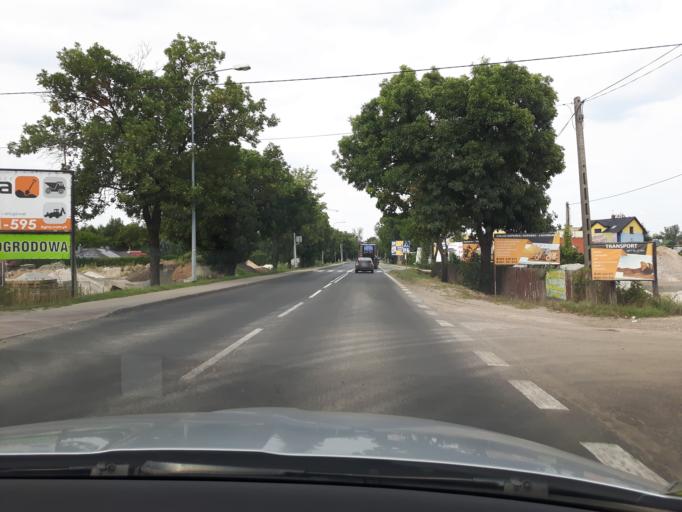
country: PL
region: Masovian Voivodeship
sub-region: Powiat legionowski
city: Stanislawow Pierwszy
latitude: 52.3428
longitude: 21.0286
